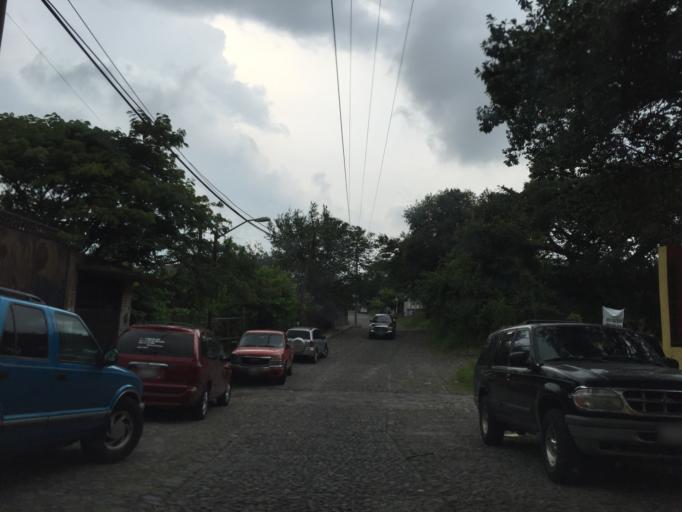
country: MX
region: Colima
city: Comala
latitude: 19.3300
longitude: -103.7617
